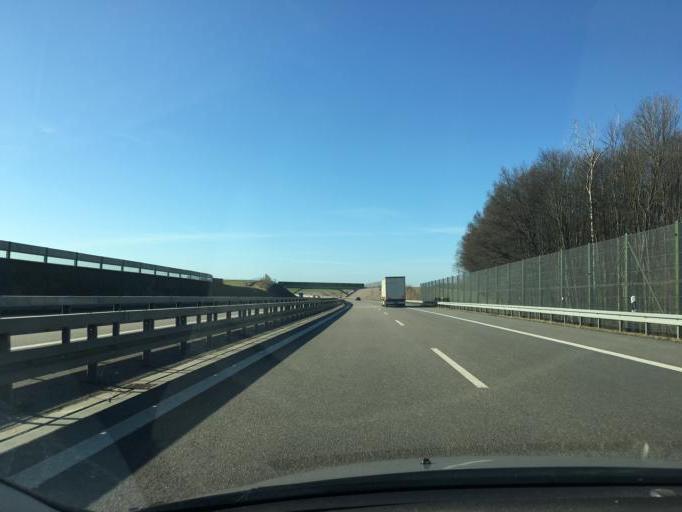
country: DE
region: Saxony
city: Narsdorf
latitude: 51.0199
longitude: 12.6839
